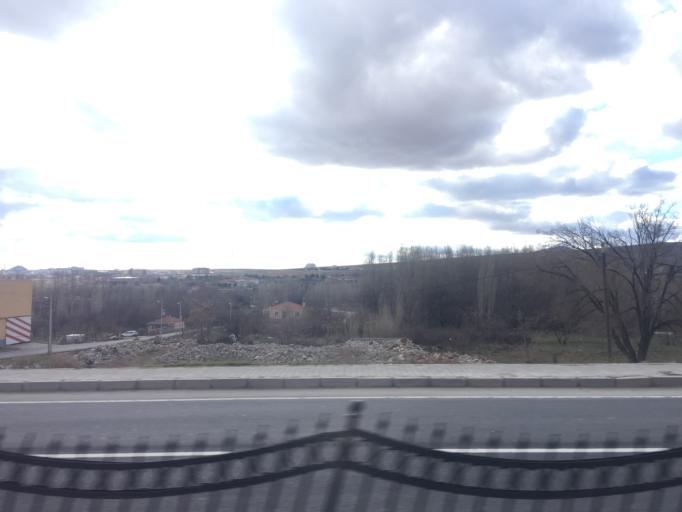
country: TR
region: Kirsehir
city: Kirsehir
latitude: 39.1675
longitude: 34.1519
